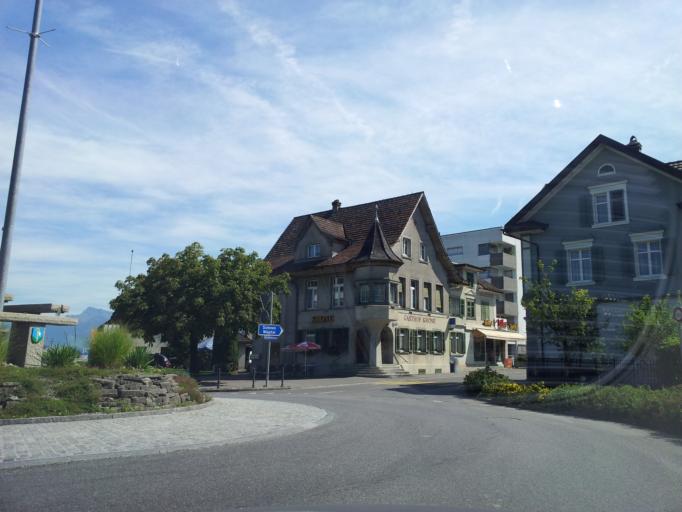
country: CH
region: Schwyz
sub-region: Bezirk March
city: Schubelbach
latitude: 47.1913
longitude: 8.8954
